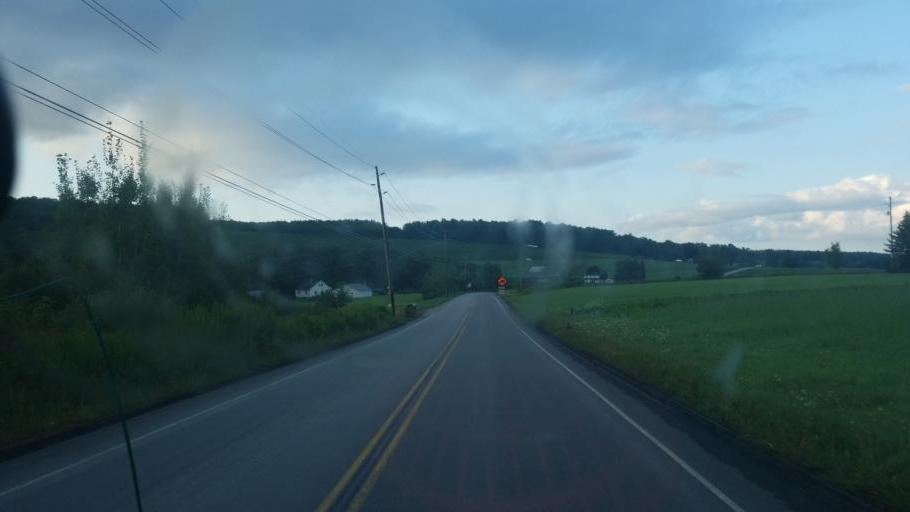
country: US
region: Pennsylvania
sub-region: Potter County
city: Galeton
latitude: 41.8584
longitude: -77.7669
